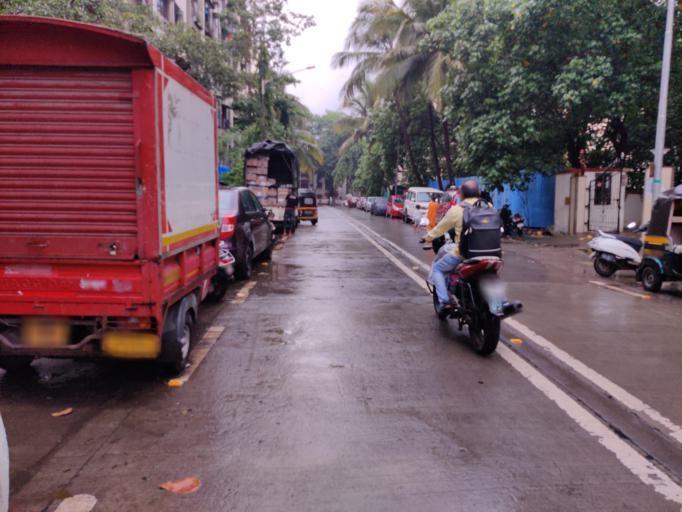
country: IN
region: Maharashtra
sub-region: Mumbai Suburban
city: Borivli
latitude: 19.2507
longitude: 72.8549
